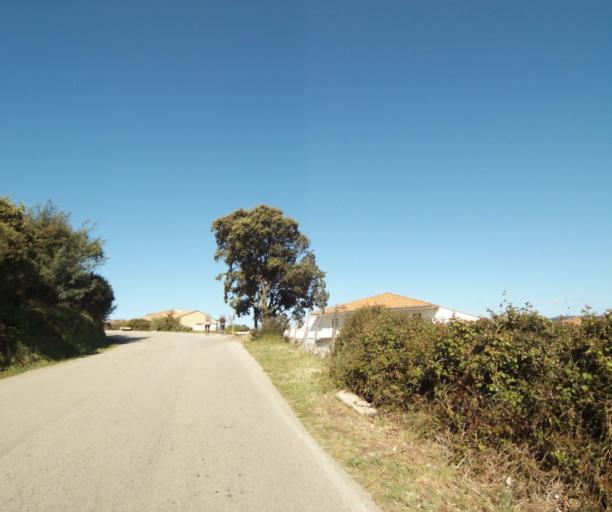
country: FR
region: Corsica
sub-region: Departement de la Corse-du-Sud
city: Propriano
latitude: 41.6700
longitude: 8.9041
